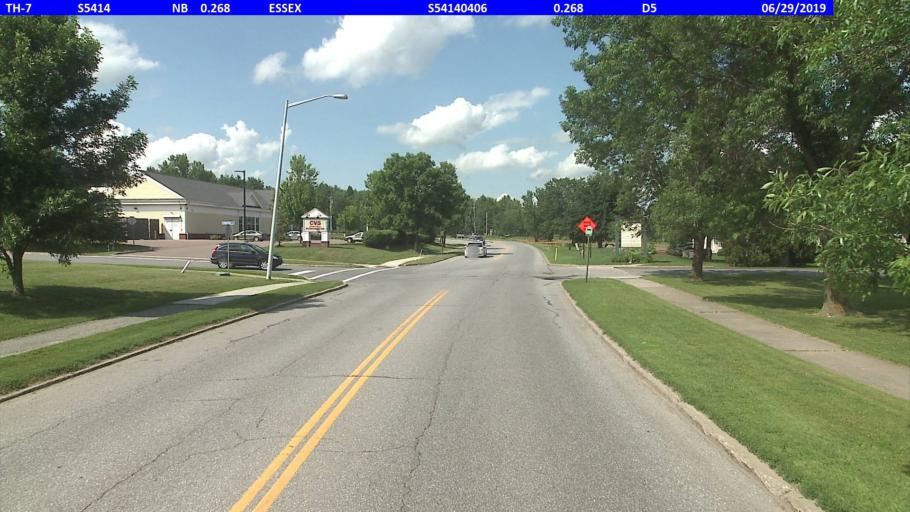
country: US
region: Vermont
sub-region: Chittenden County
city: Essex Junction
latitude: 44.5083
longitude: -73.0789
